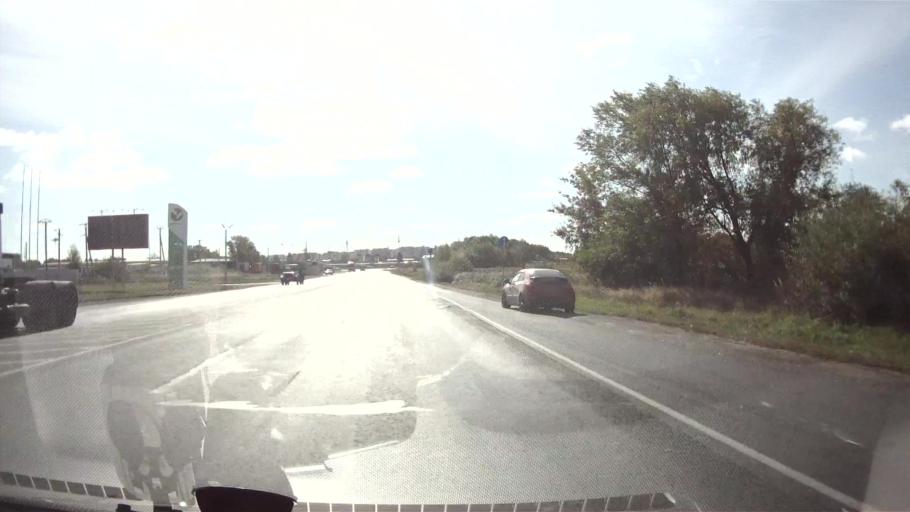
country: RU
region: Ulyanovsk
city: Isheyevka
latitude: 54.2950
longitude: 48.2504
